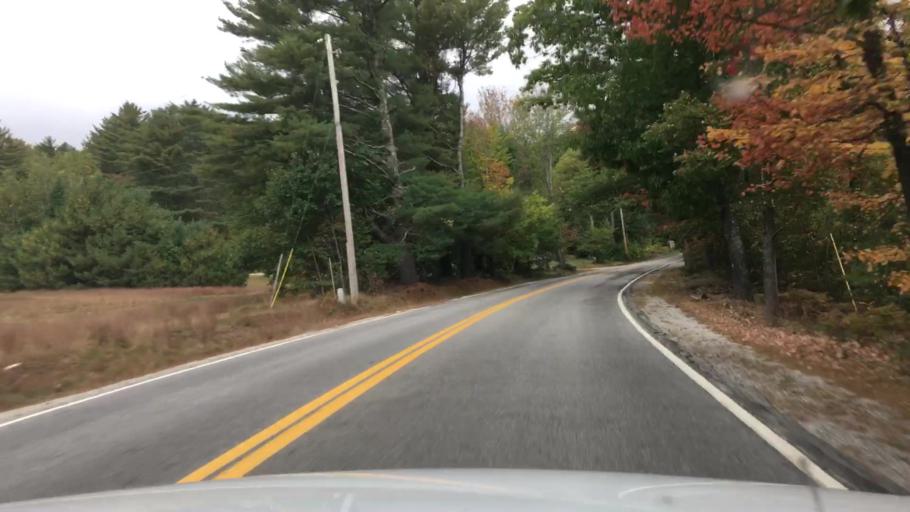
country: US
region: Maine
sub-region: Oxford County
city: Bethel
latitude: 44.3486
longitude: -70.7892
